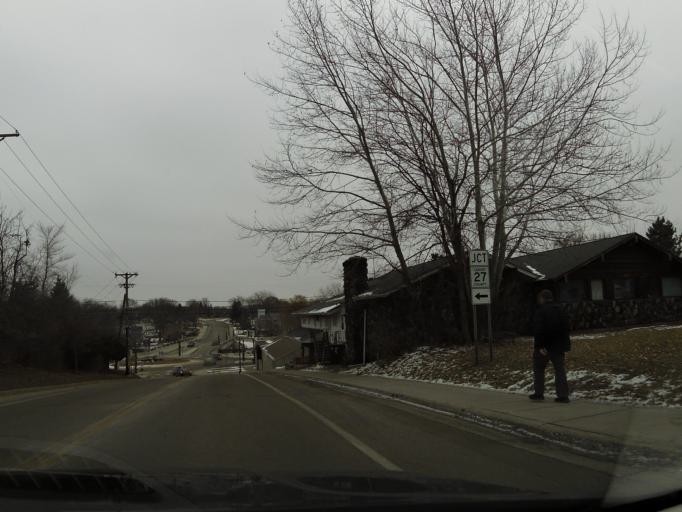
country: US
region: Minnesota
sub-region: Carver County
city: Watertown
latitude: 44.9642
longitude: -93.8485
